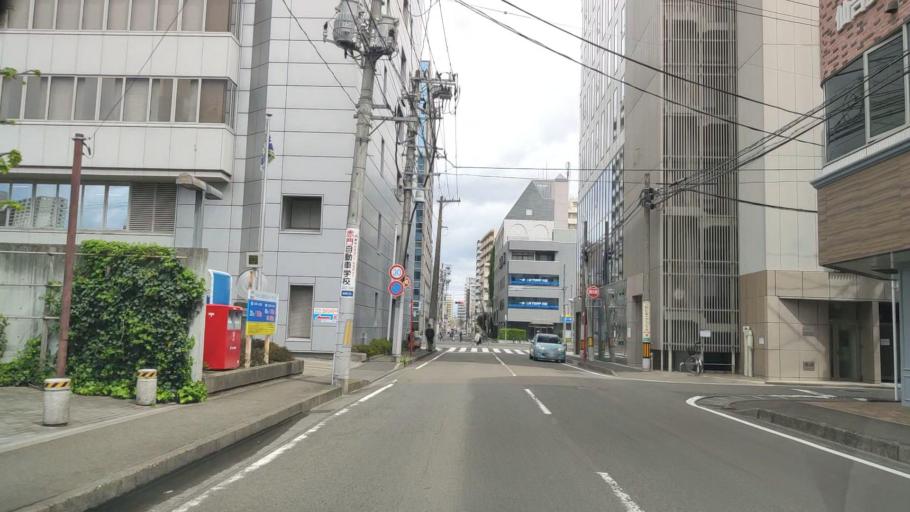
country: JP
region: Miyagi
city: Sendai-shi
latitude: 38.2586
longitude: 140.8890
